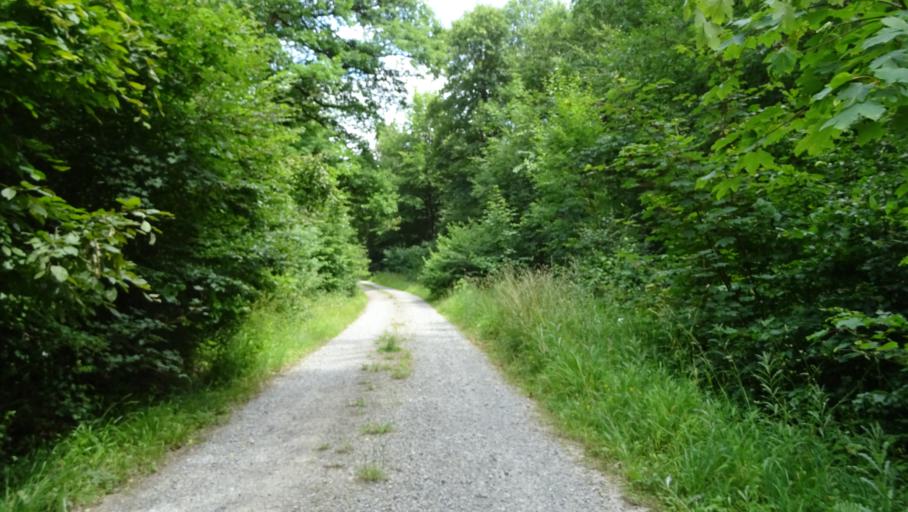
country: DE
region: Baden-Wuerttemberg
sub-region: Karlsruhe Region
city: Obrigheim
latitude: 49.3876
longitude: 9.1109
